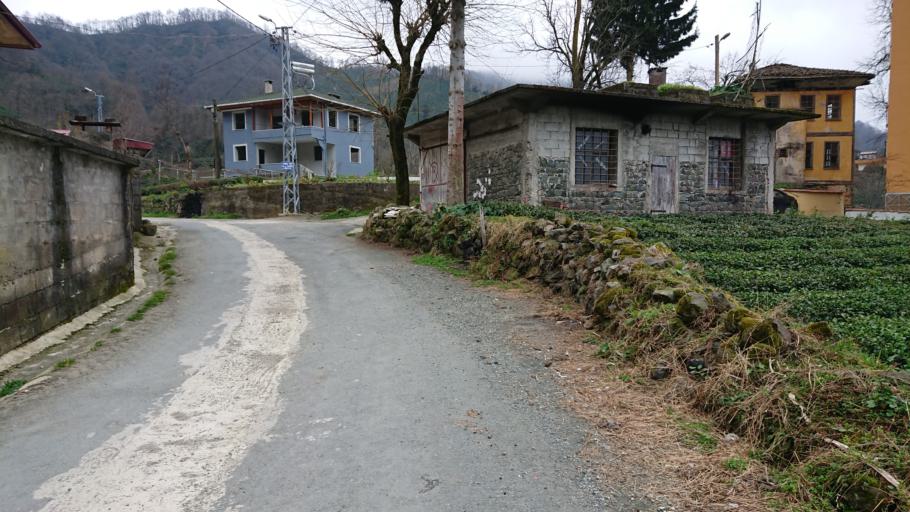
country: TR
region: Rize
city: Rize
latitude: 40.9815
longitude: 40.4952
